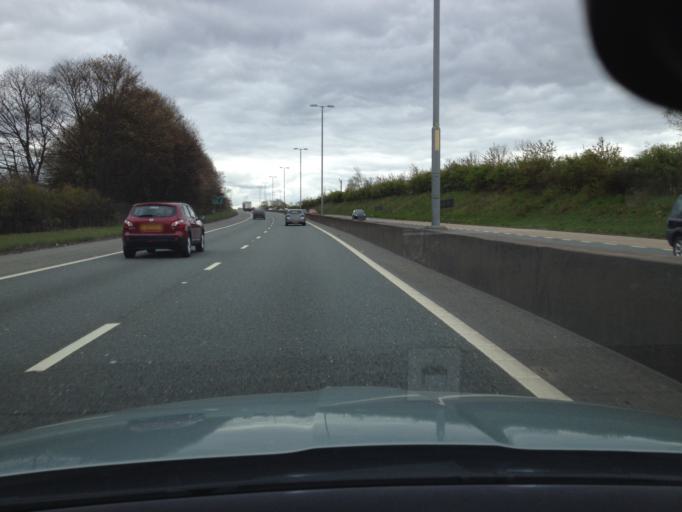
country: GB
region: Scotland
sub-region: North Lanarkshire
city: Coatbridge
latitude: 55.8447
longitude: -4.0536
